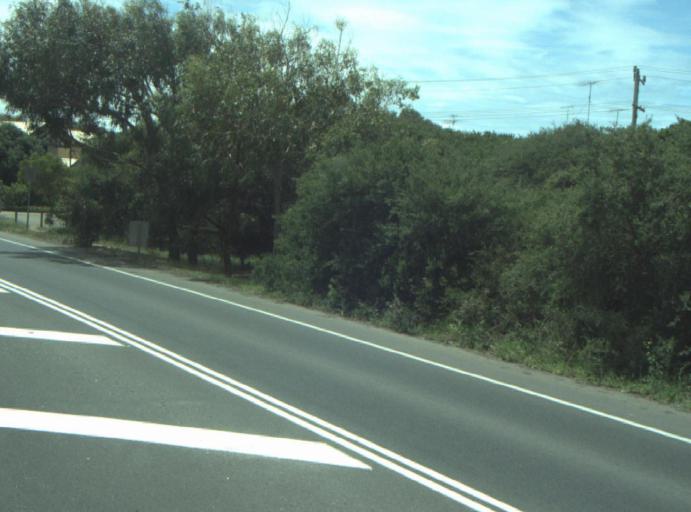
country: AU
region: Victoria
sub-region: Greater Geelong
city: Leopold
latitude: -38.2707
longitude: 144.5133
